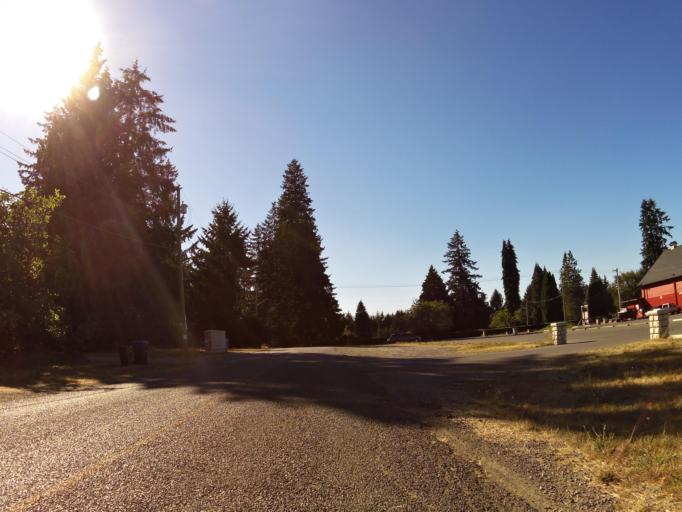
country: CA
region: British Columbia
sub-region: Cowichan Valley Regional District
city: Ladysmith
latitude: 49.0865
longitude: -123.8495
